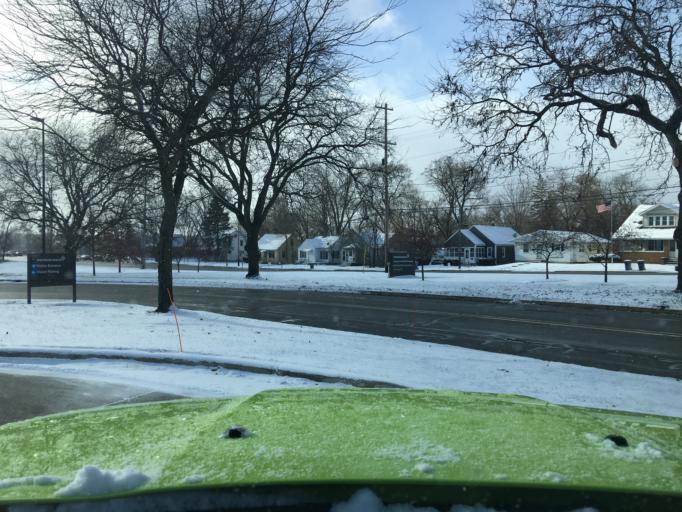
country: US
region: Michigan
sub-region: Kent County
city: Grand Rapids
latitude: 42.9759
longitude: -85.6391
